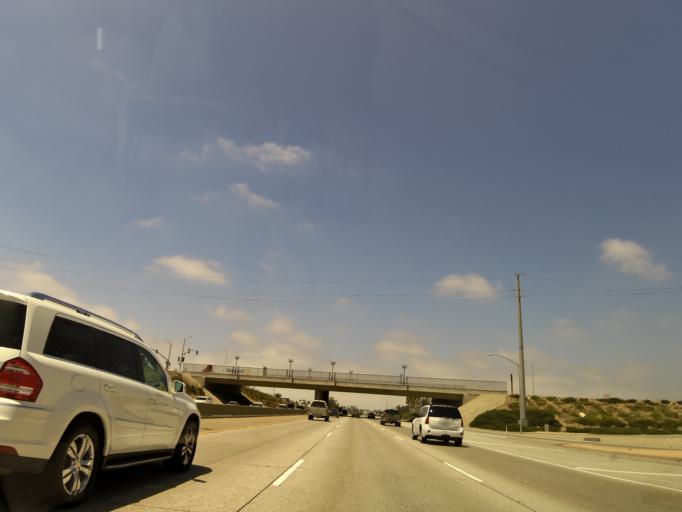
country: US
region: California
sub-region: Ventura County
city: El Rio
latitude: 34.2226
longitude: -119.1408
